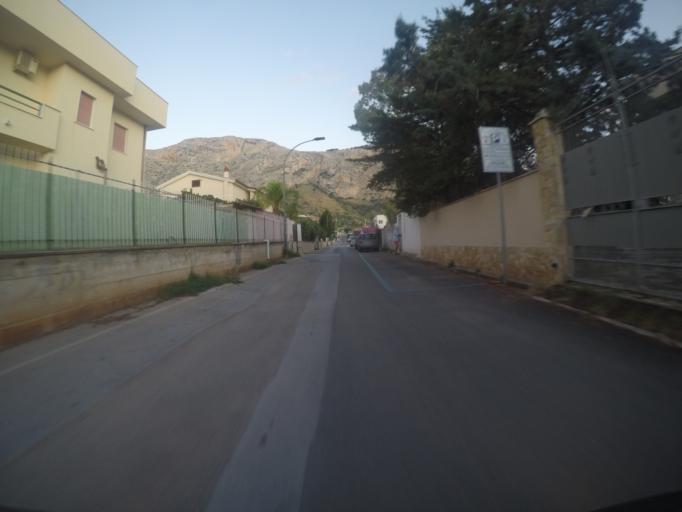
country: IT
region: Sicily
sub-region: Palermo
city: Isola delle Femmine
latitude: 38.1848
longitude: 13.2410
